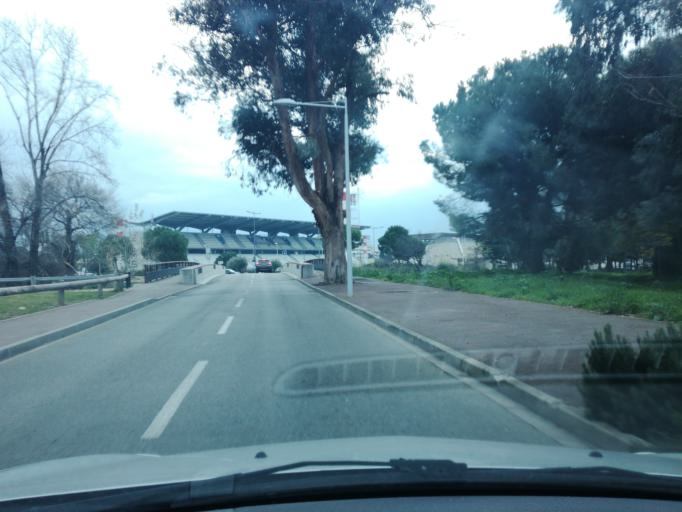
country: FR
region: Provence-Alpes-Cote d'Azur
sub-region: Departement des Alpes-Maritimes
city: Mandelieu-la-Napoule
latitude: 43.5546
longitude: 6.9633
